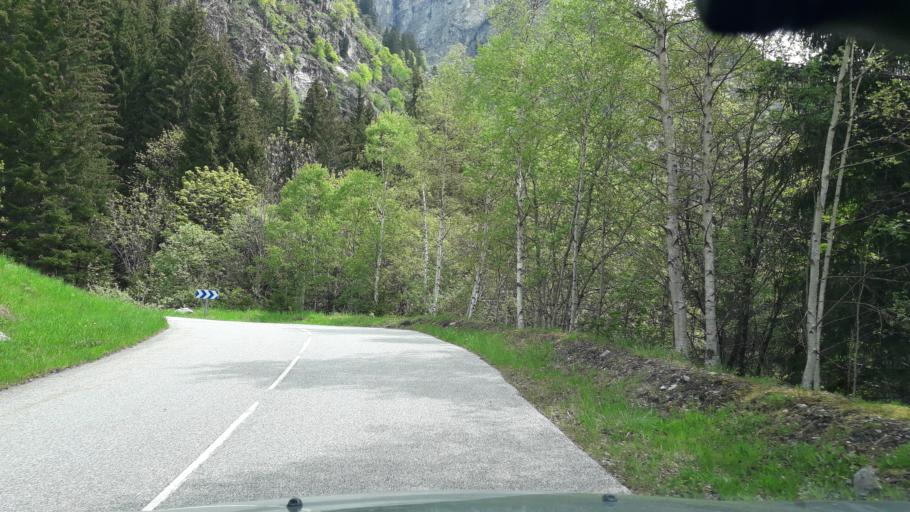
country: FR
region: Rhone-Alpes
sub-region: Departement de l'Isere
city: Theys
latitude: 45.2099
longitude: 6.0568
